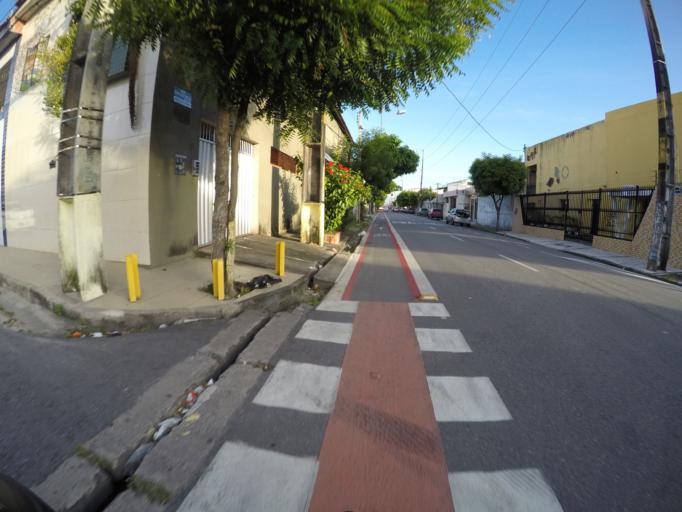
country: BR
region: Ceara
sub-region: Fortaleza
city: Fortaleza
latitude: -3.7550
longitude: -38.5134
